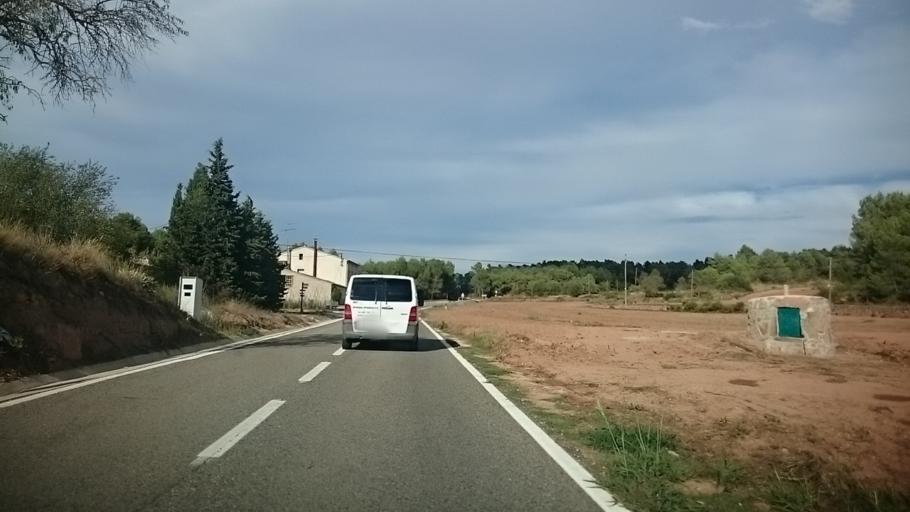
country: ES
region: Catalonia
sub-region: Provincia de Barcelona
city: Odena
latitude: 41.6235
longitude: 1.6576
